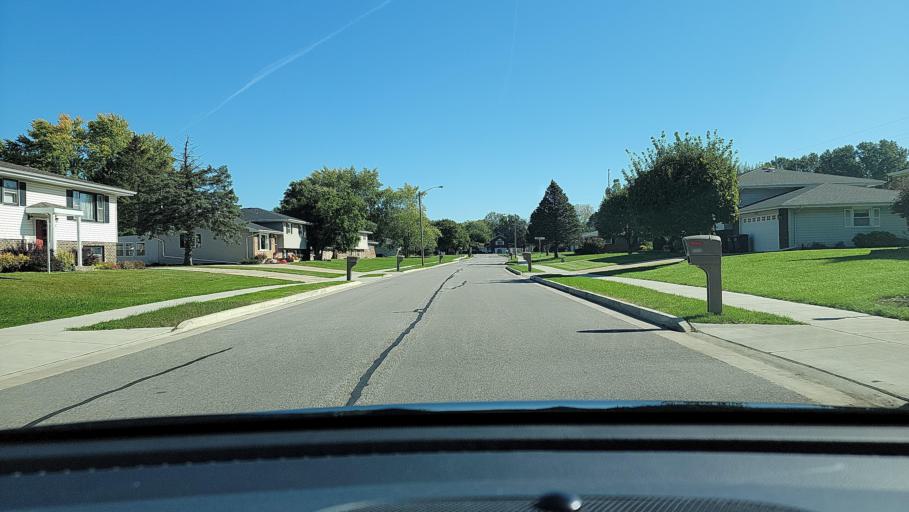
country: US
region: Indiana
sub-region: Porter County
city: Portage
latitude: 41.5724
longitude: -87.1665
